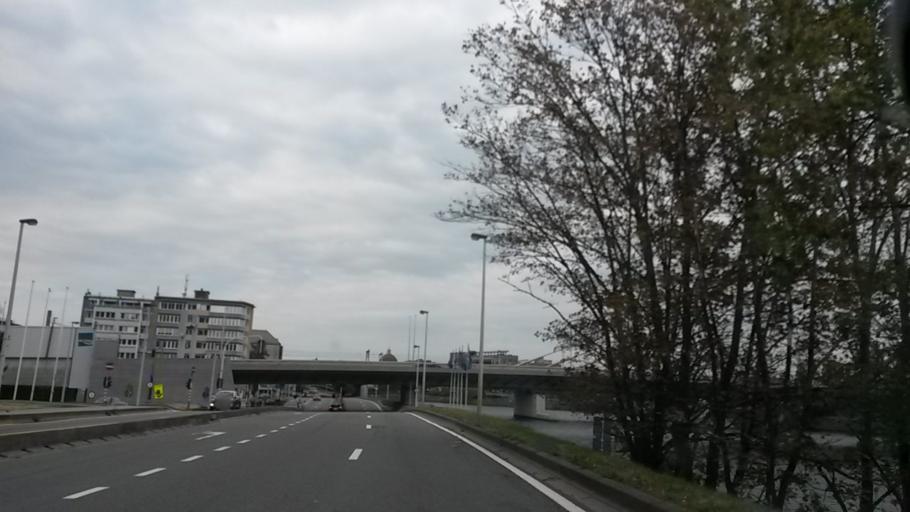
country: BE
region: Wallonia
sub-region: Province de Liege
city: Liege
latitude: 50.6153
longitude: 5.5772
